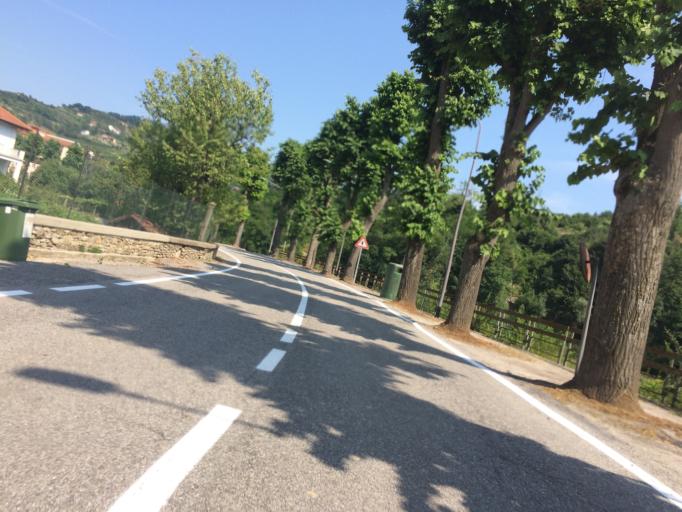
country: IT
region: Piedmont
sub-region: Provincia di Cuneo
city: Cortemilia
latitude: 44.5778
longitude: 8.1887
